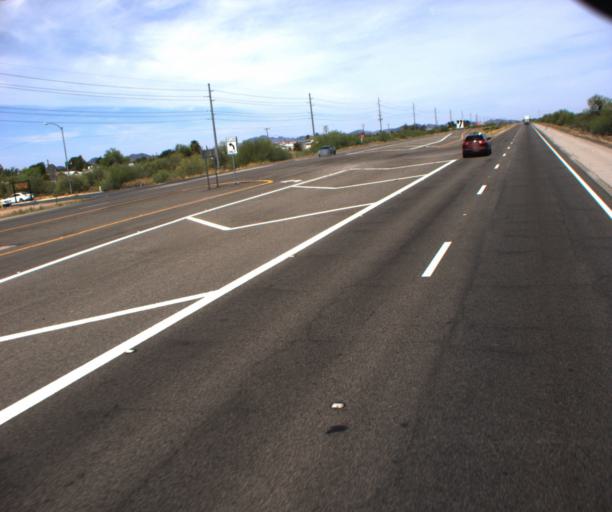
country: US
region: Arizona
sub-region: Maricopa County
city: Wickenburg
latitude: 33.8167
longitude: -112.5782
